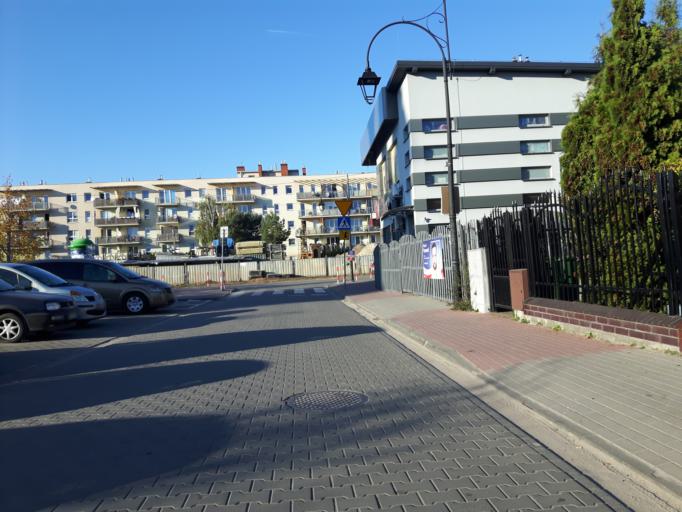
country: PL
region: Masovian Voivodeship
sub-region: Powiat wolominski
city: Zabki
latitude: 52.2790
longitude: 21.1272
